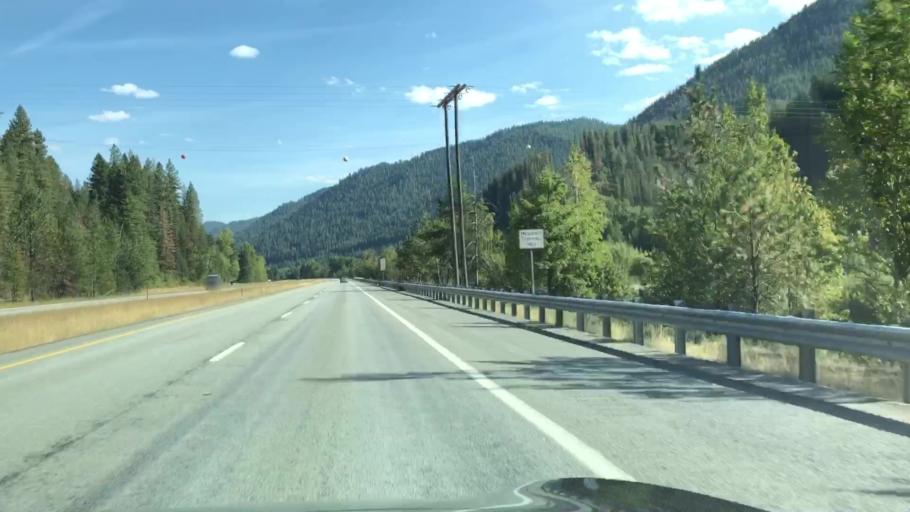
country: US
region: Idaho
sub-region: Shoshone County
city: Osburn
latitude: 47.5219
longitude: -116.0418
